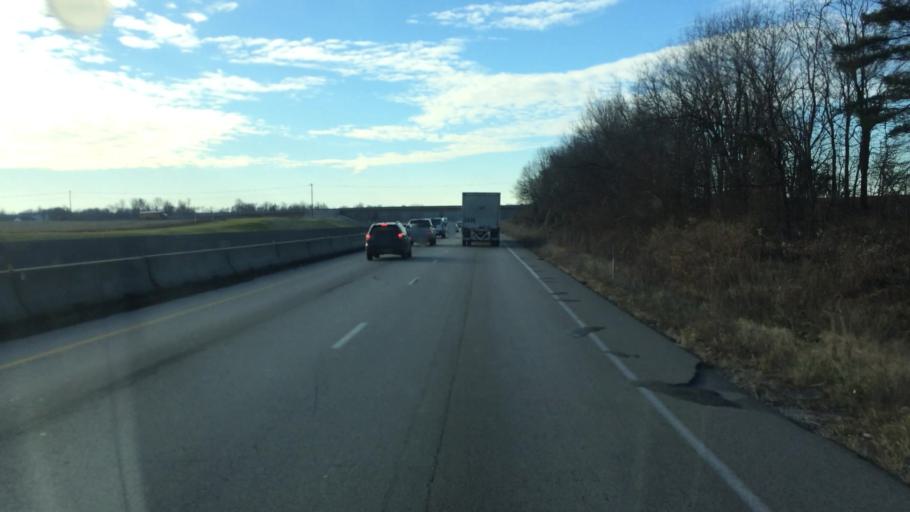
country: US
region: Kentucky
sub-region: Hardin County
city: Elizabethtown
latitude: 37.5766
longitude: -85.8731
